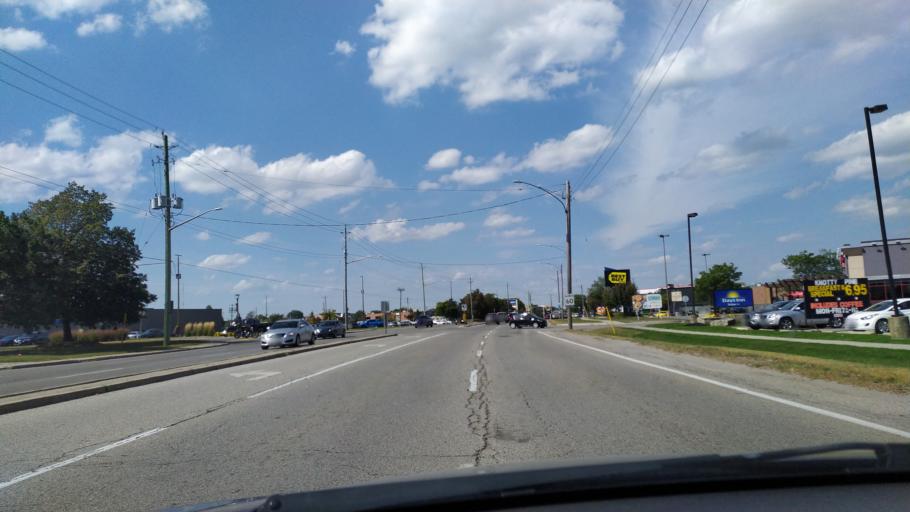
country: CA
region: Ontario
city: London
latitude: 42.9320
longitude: -81.2217
